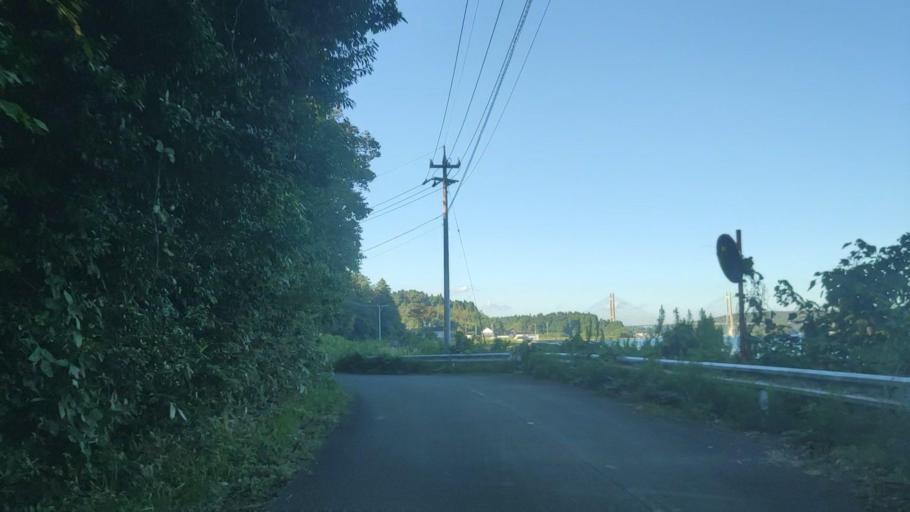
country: JP
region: Ishikawa
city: Nanao
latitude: 37.1251
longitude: 136.8960
